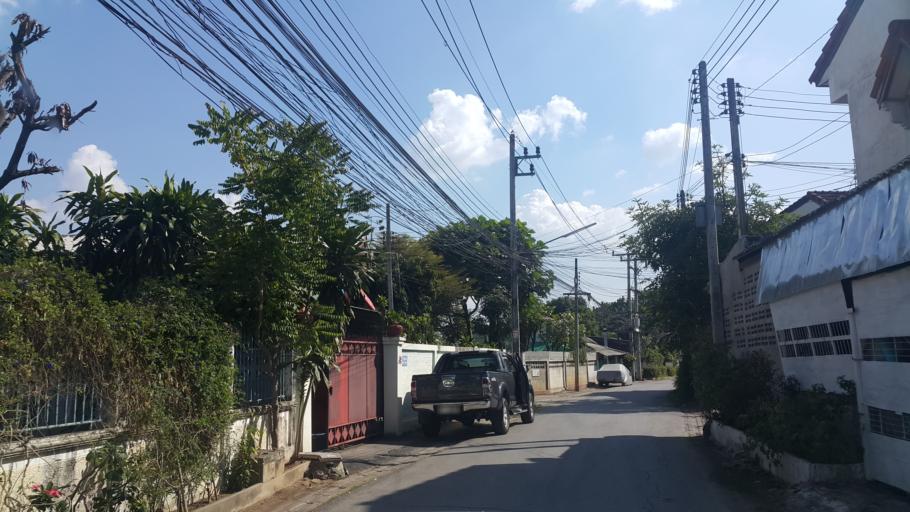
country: TH
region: Chiang Mai
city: Chiang Mai
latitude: 18.7713
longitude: 99.0136
